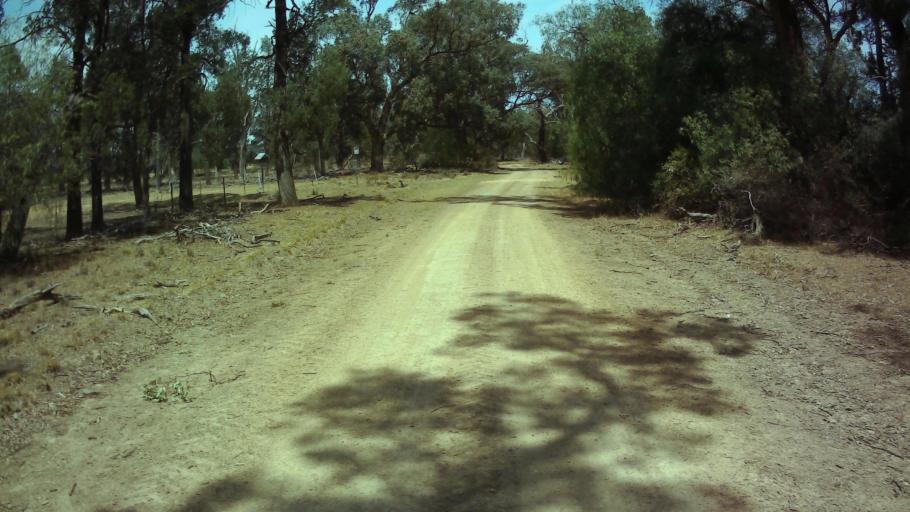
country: AU
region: New South Wales
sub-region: Weddin
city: Grenfell
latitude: -34.0308
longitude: 147.9343
